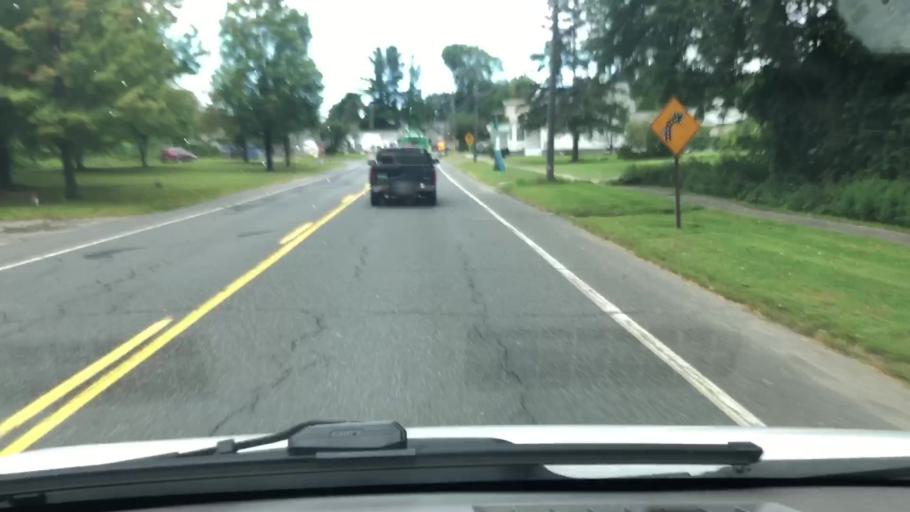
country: US
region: Massachusetts
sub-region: Franklin County
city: Turners Falls
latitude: 42.5982
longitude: -72.5503
